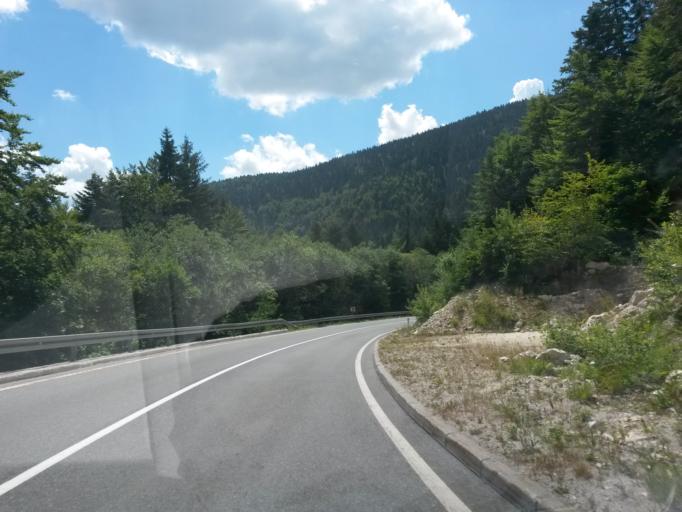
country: BA
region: Federation of Bosnia and Herzegovina
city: Bugojno
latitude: 44.0252
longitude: 17.3020
